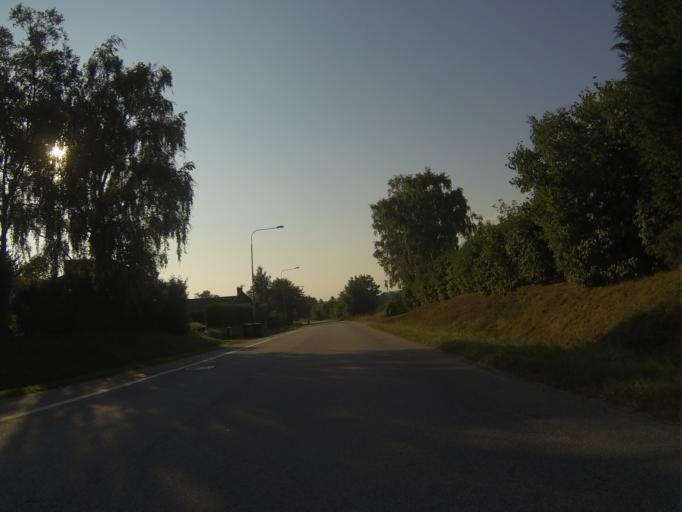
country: SE
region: Skane
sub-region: Lunds Kommun
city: Genarp
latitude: 55.6610
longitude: 13.3648
